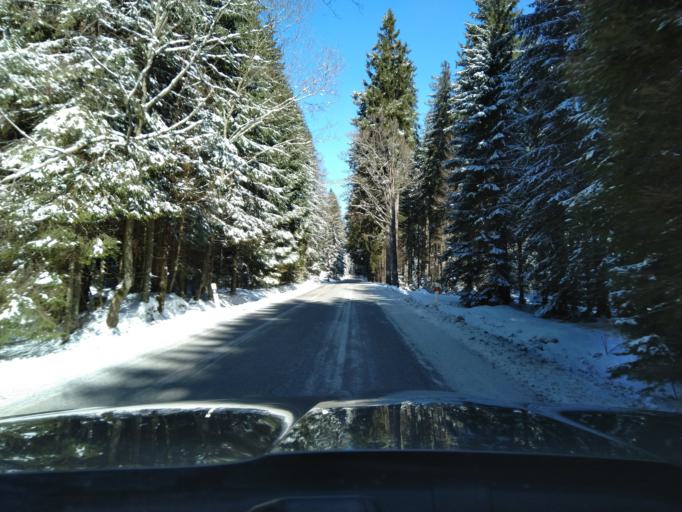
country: CZ
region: Jihocesky
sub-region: Okres Prachatice
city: Zdikov
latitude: 49.0531
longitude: 13.6597
